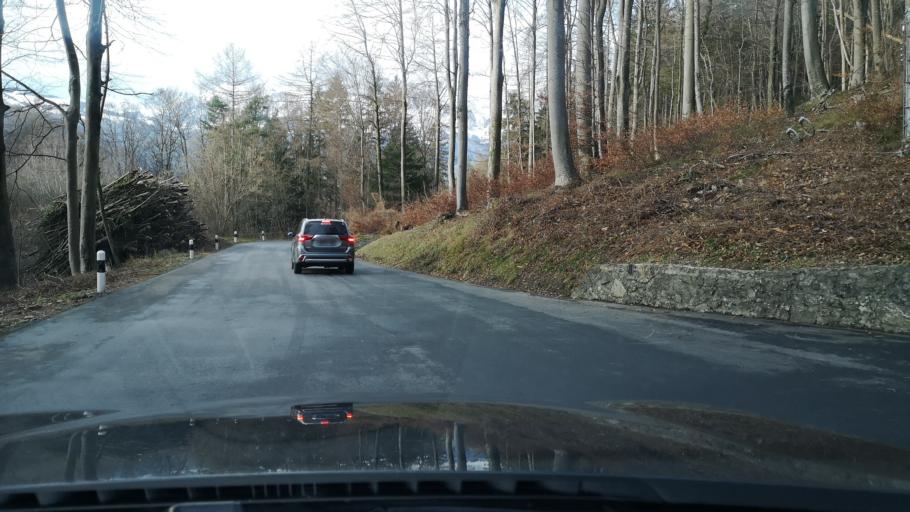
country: LI
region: Vaduz
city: Vaduz
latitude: 47.1341
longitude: 9.5291
